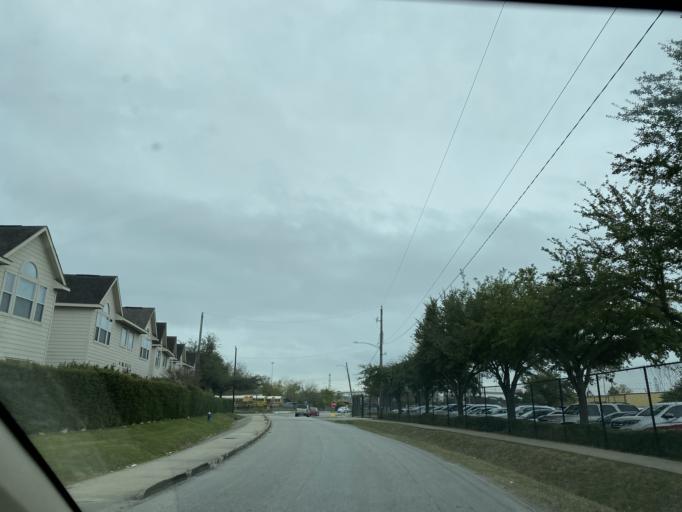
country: US
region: Texas
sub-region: Harris County
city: Piney Point Village
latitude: 29.7292
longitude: -95.4922
